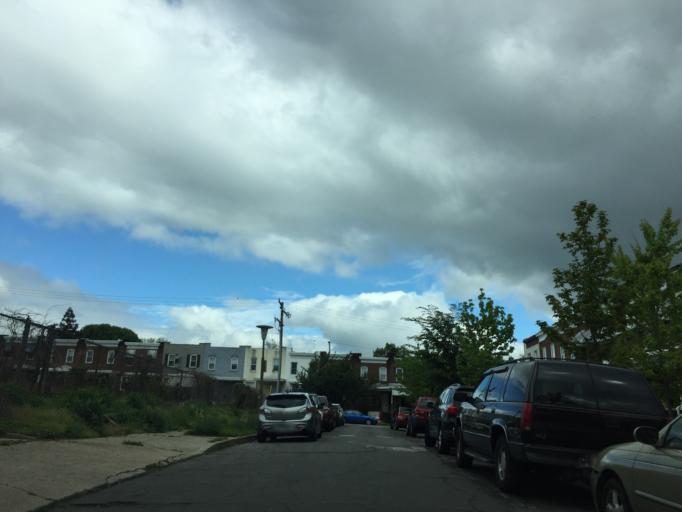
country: US
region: Maryland
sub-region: City of Baltimore
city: Baltimore
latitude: 39.3256
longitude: -76.6300
